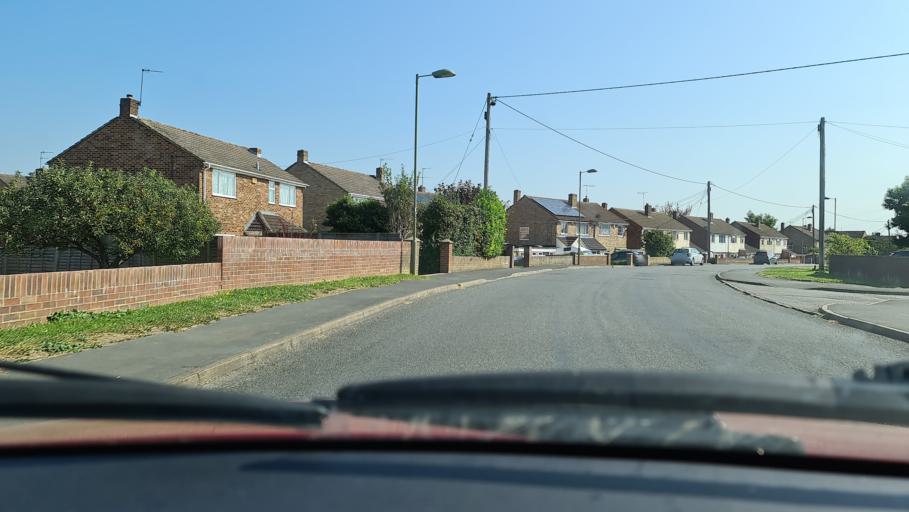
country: GB
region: England
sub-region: Oxfordshire
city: Bicester
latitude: 51.9066
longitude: -1.1627
